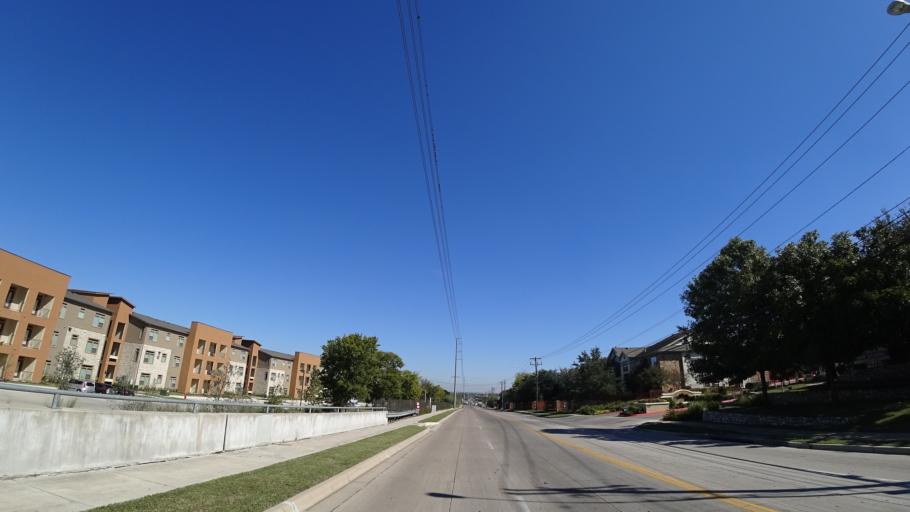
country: US
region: Texas
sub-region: Travis County
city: Austin
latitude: 30.2223
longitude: -97.7052
